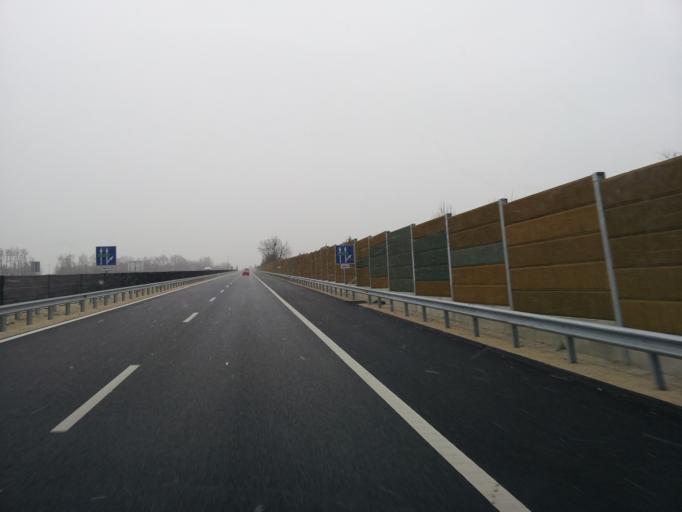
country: HU
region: Veszprem
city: Herend
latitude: 47.1337
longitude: 17.7370
